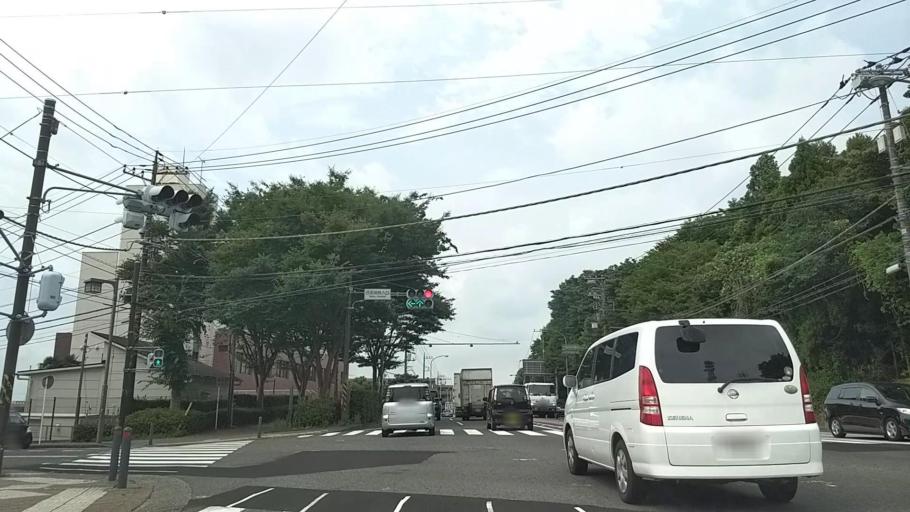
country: JP
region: Kanagawa
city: Minami-rinkan
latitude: 35.4744
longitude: 139.5012
